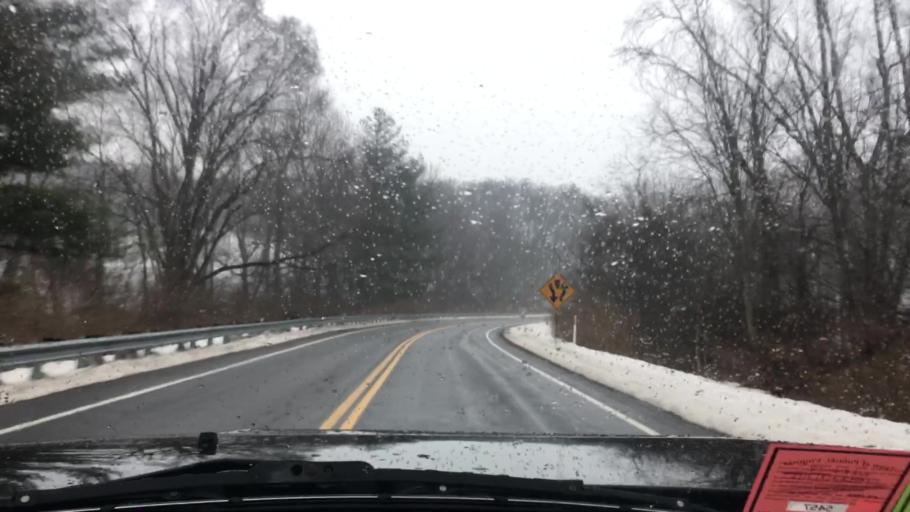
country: US
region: Virginia
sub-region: Pulaski County
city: Pulaski
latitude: 36.9991
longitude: -80.7948
